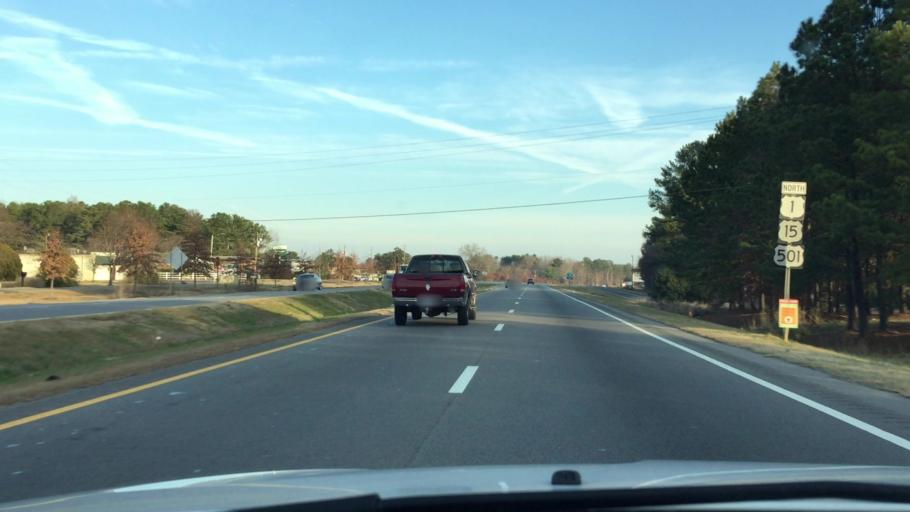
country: US
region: North Carolina
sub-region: Lee County
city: Sanford
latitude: 35.4451
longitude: -79.2148
